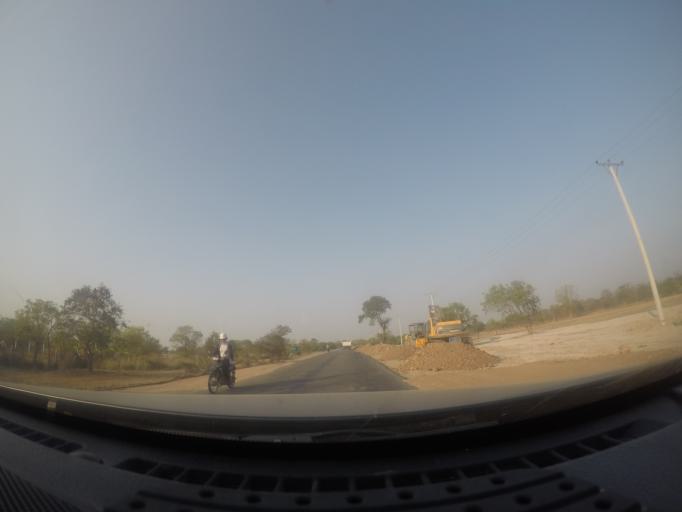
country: MM
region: Mandalay
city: Yamethin
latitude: 20.6268
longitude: 96.0832
